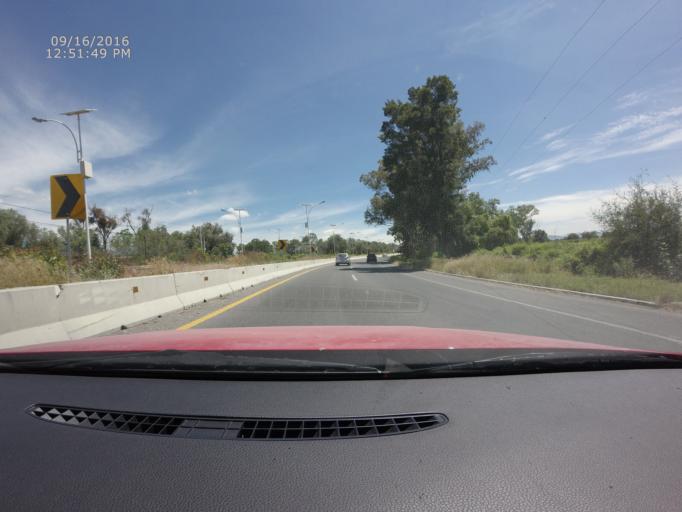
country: MX
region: Queretaro
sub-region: Colon
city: Purisima de Cubos (La Purisima)
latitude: 20.6166
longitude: -100.1518
